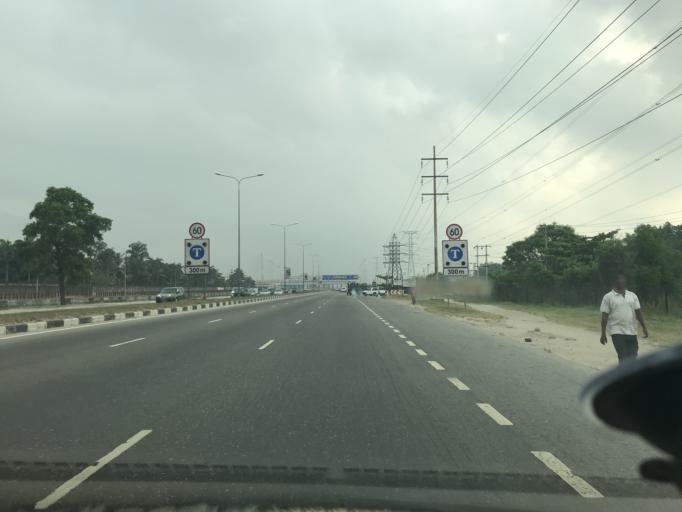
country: NG
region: Lagos
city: Ikoyi
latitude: 6.4426
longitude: 3.5341
